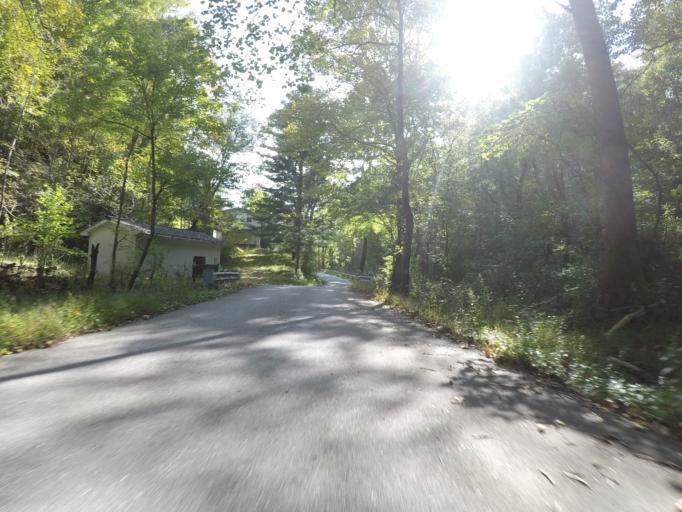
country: US
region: West Virginia
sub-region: Wayne County
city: Lavalette
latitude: 38.3624
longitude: -82.4845
